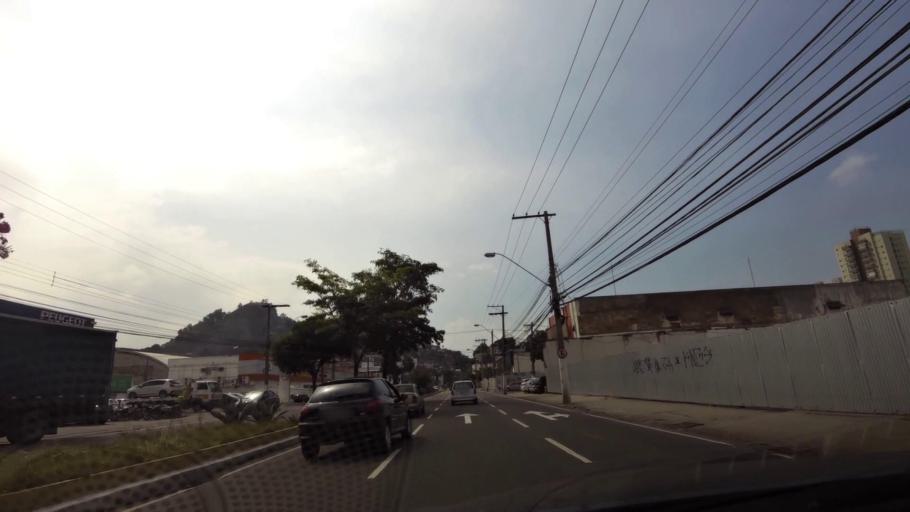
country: BR
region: Espirito Santo
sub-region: Vitoria
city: Vitoria
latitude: -20.3106
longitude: -40.3127
